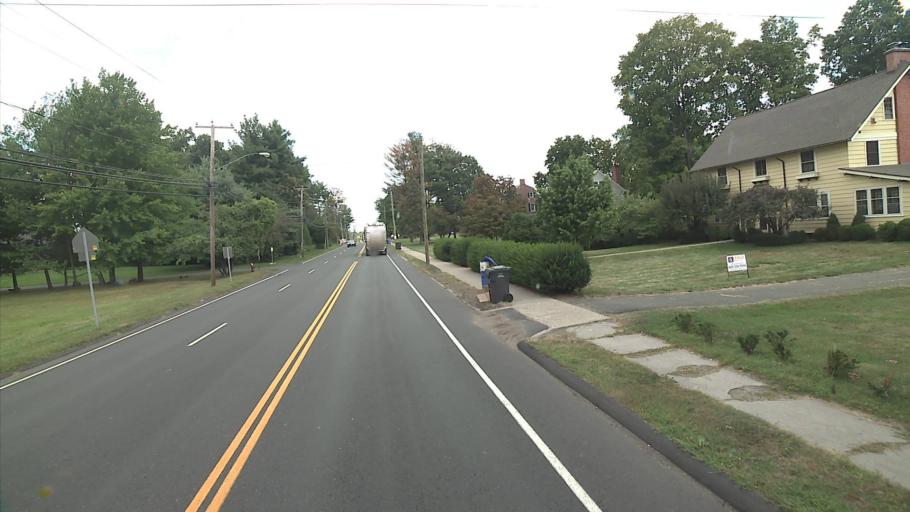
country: US
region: Connecticut
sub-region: Hartford County
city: Blue Hills
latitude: 41.7909
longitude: -72.7152
